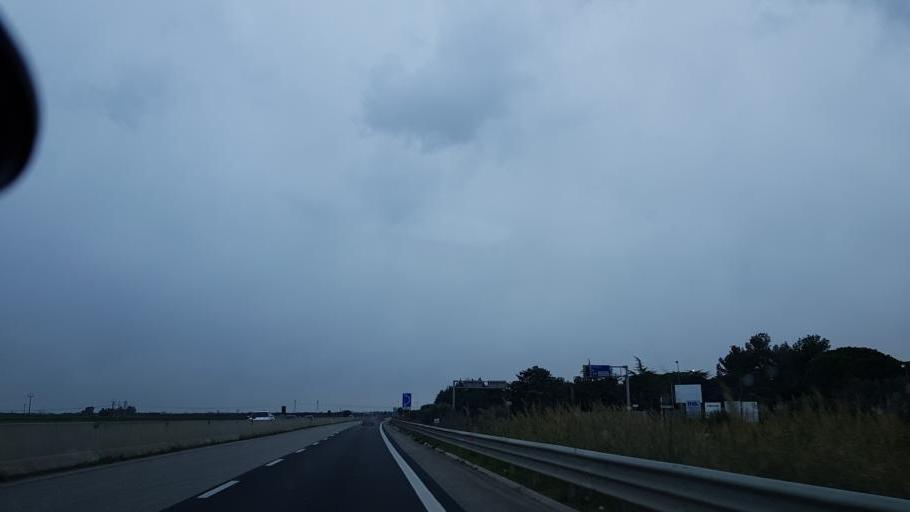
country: IT
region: Apulia
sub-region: Provincia di Brindisi
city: Mesagne
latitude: 40.5863
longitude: 17.8520
